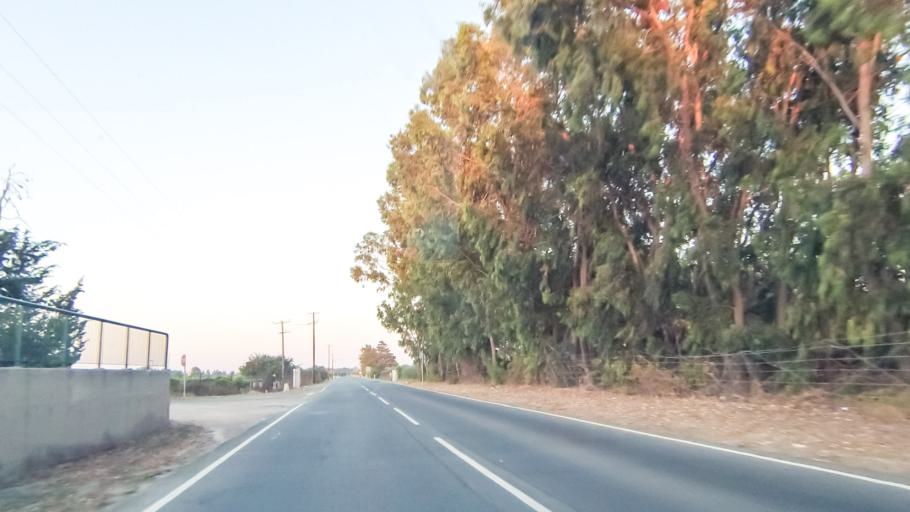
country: CY
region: Larnaka
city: Kolossi
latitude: 34.6556
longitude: 32.9309
